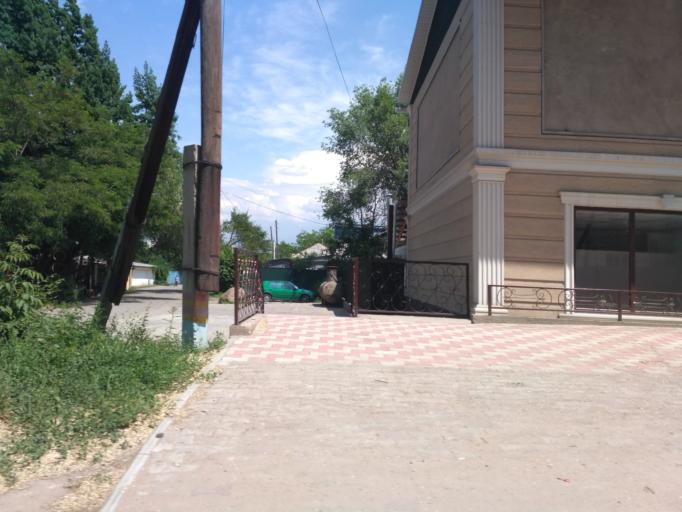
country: KZ
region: Almaty Oblysy
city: Burunday
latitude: 43.1893
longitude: 76.6203
